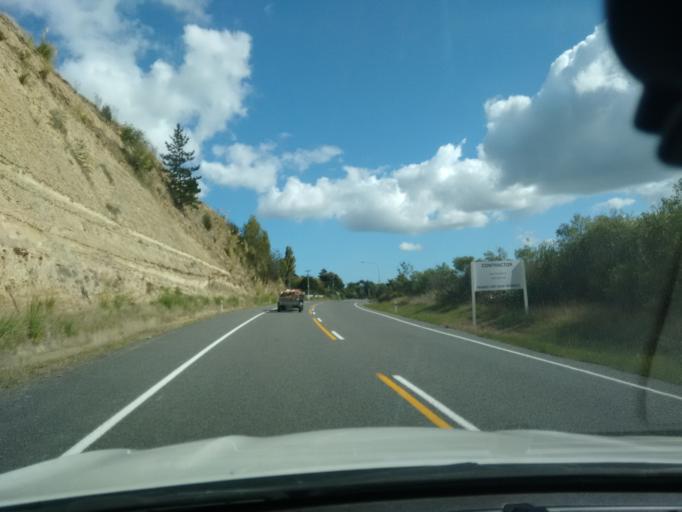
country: NZ
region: Manawatu-Wanganui
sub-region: Wanganui District
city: Wanganui
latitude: -39.8972
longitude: 175.0917
